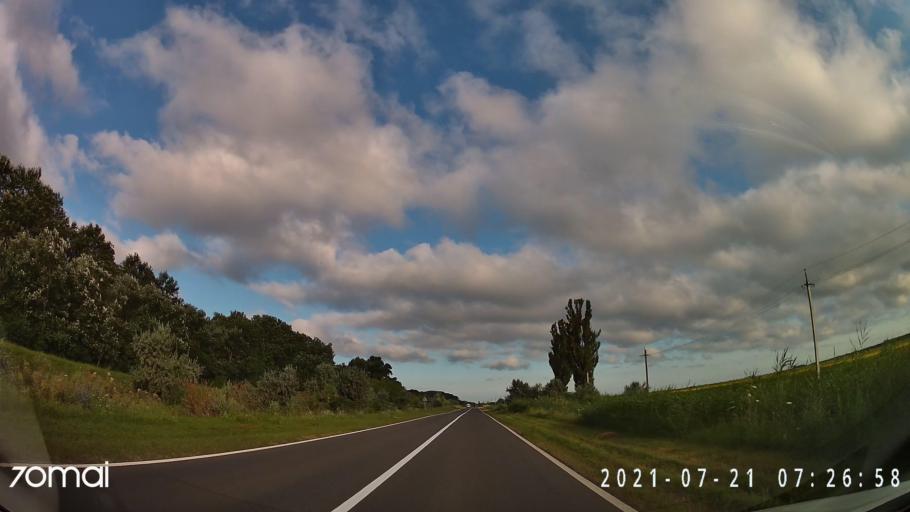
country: RO
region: Tulcea
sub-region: Oras Isaccea
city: Isaccea
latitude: 45.3005
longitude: 28.4272
